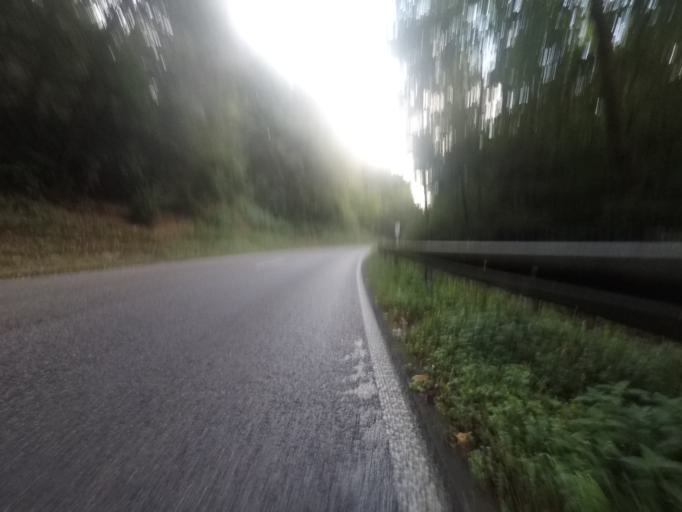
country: DE
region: Baden-Wuerttemberg
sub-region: Karlsruhe Region
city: Ettlingen
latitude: 48.9152
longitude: 8.3992
